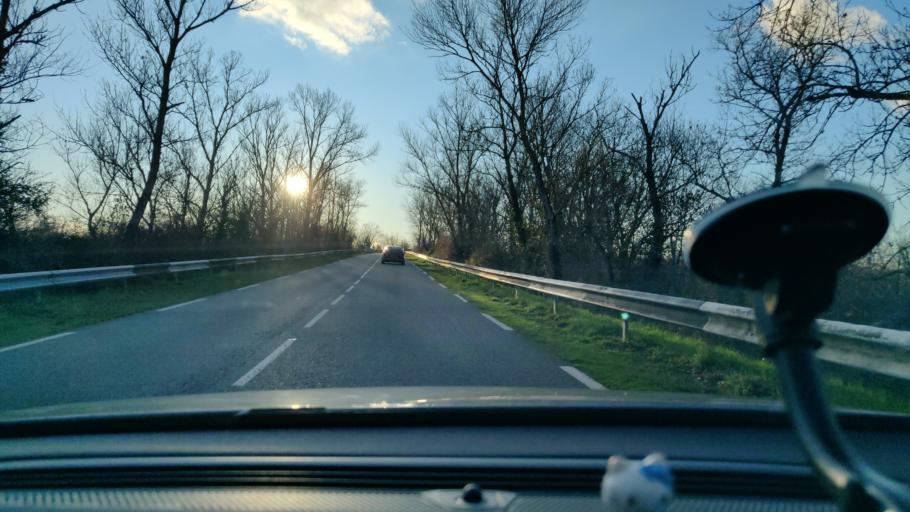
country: FR
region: Midi-Pyrenees
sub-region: Departement de la Haute-Garonne
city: Labarthe-sur-Leze
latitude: 43.4613
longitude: 1.4232
